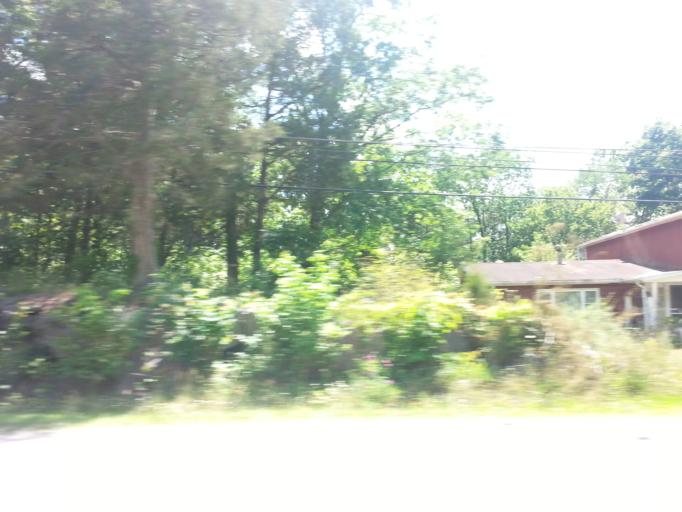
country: US
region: Virginia
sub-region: Lee County
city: Pennington Gap
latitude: 36.7229
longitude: -82.9857
